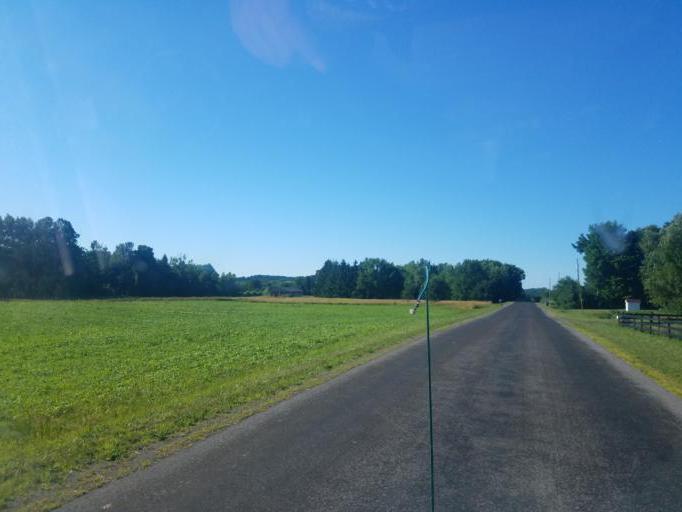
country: US
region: New York
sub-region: Wayne County
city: Lyons
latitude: 43.0987
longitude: -77.0095
